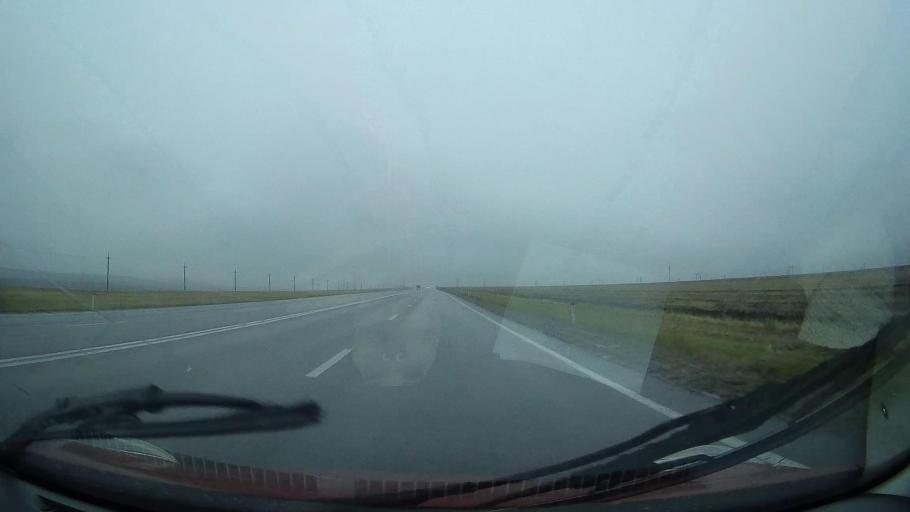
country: RU
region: Stavropol'skiy
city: Kursavka
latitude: 44.5806
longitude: 42.2451
